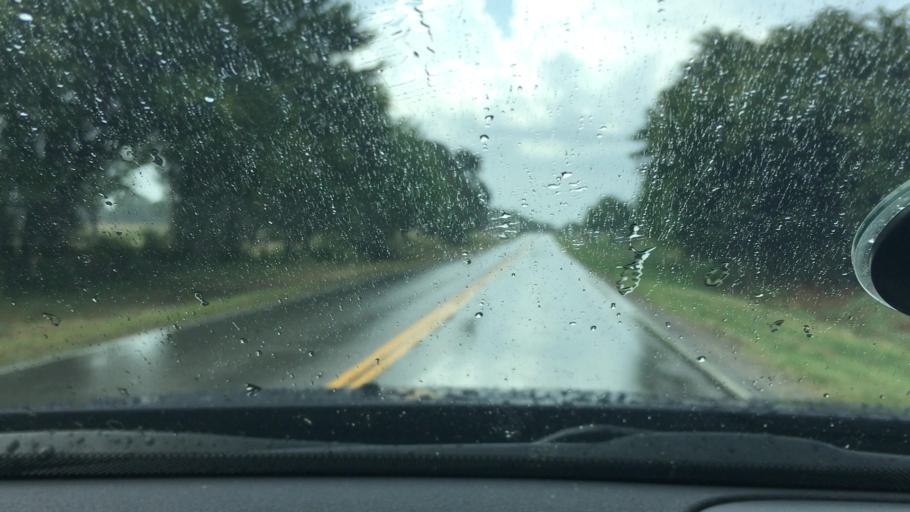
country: US
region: Oklahoma
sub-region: Johnston County
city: Tishomingo
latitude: 34.1821
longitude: -96.7176
